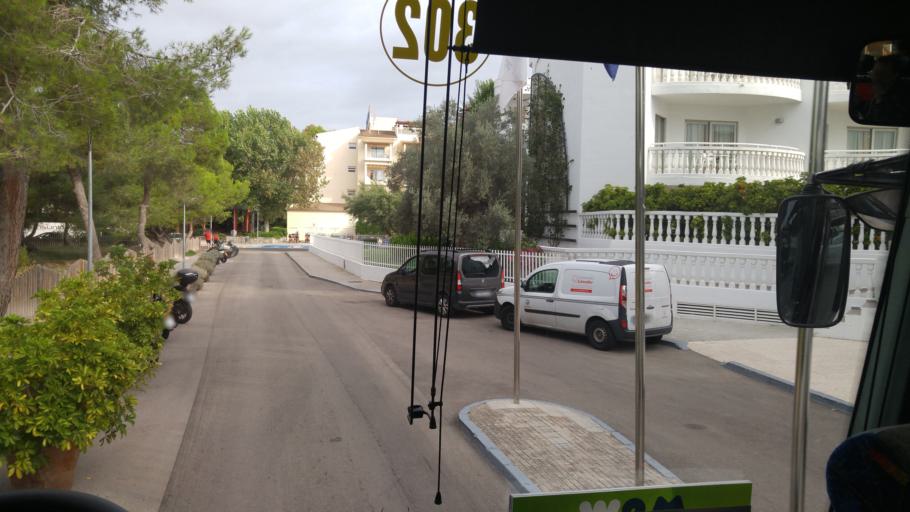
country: ES
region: Balearic Islands
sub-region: Illes Balears
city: Port d'Alcudia
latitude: 39.7873
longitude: 3.1272
